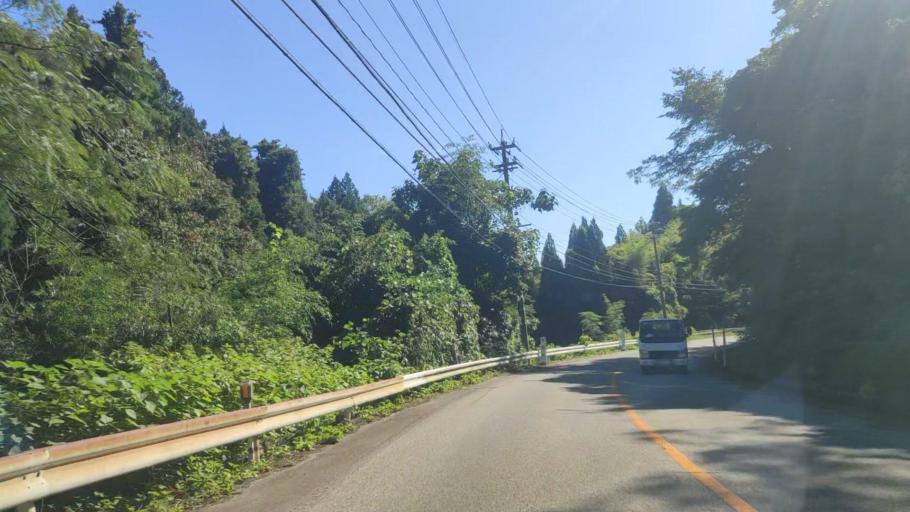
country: JP
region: Ishikawa
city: Nanao
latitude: 37.3420
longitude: 137.2295
